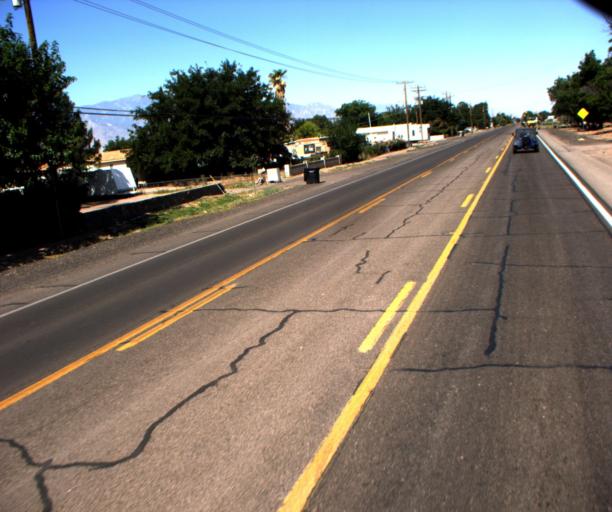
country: US
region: Arizona
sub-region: Graham County
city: Safford
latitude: 32.8167
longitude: -109.6716
